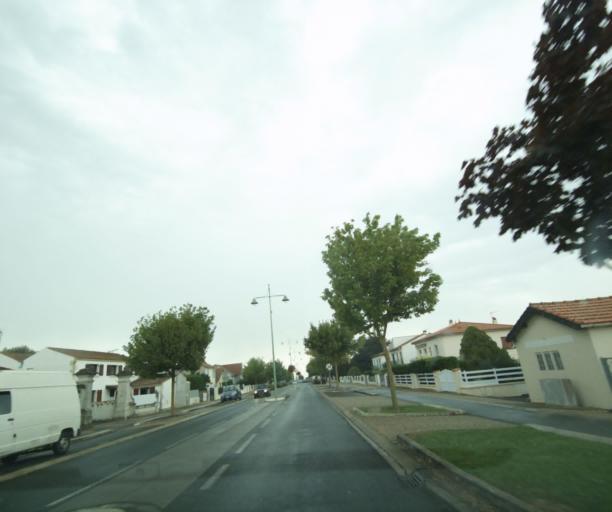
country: FR
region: Poitou-Charentes
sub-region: Departement de la Charente-Maritime
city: Tonnay-Charente
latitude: 45.9474
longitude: -0.9078
